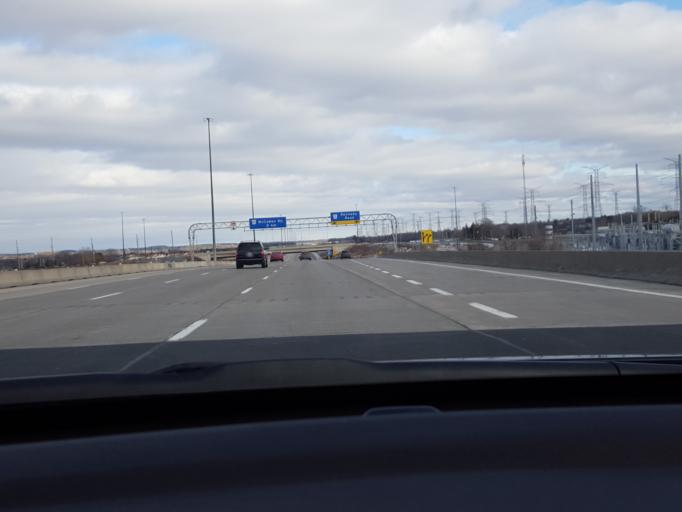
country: CA
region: Ontario
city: Markham
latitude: 43.8483
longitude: -79.3152
